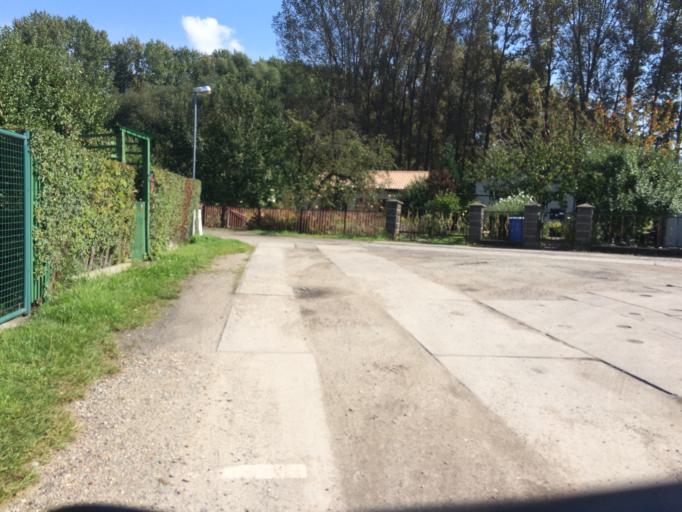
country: DE
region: Berlin
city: Heinersdorf
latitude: 52.5786
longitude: 13.4484
